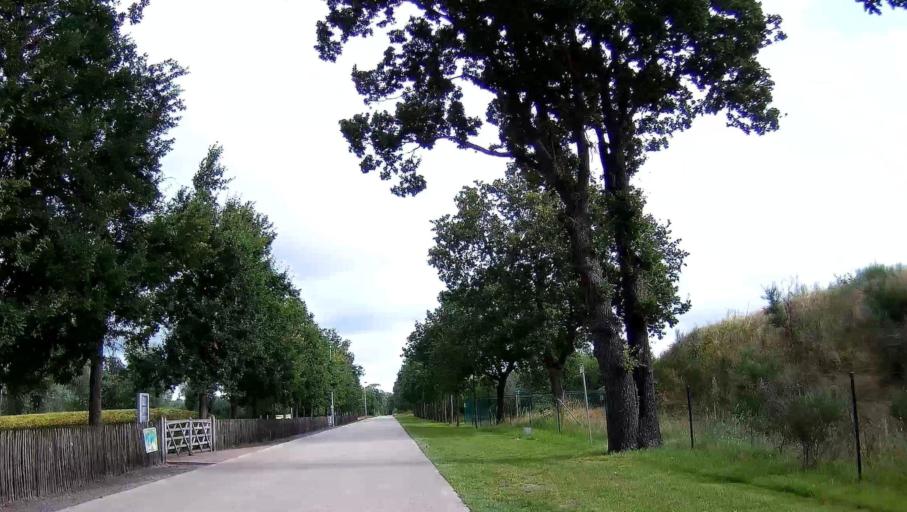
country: BE
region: Flanders
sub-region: Provincie Antwerpen
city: Balen
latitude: 51.2310
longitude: 5.2153
